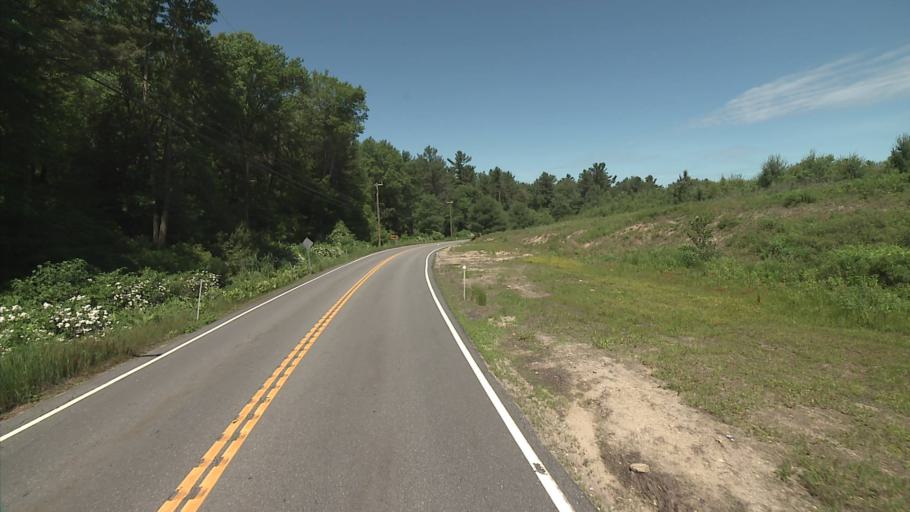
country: US
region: Rhode Island
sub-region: Washington County
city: Hopkinton
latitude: 41.5506
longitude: -71.8482
